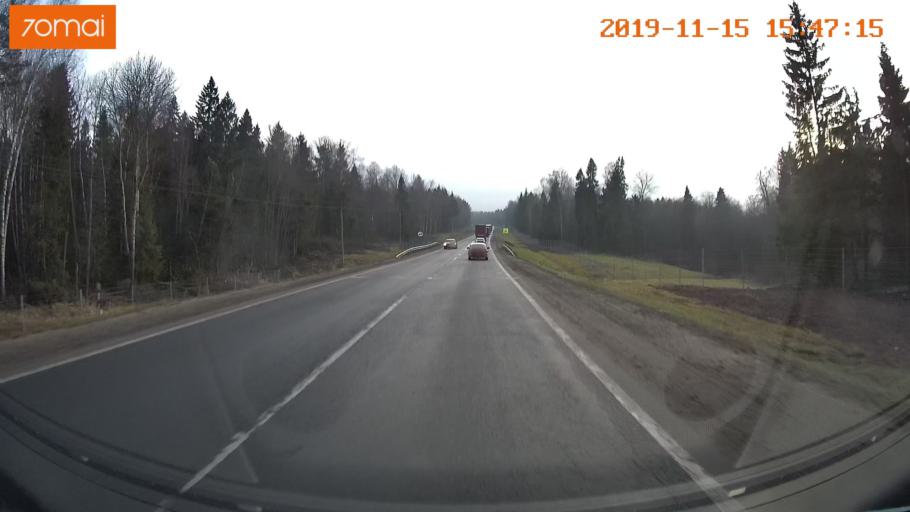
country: RU
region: Jaroslavl
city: Danilov
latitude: 57.9402
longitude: 40.0111
